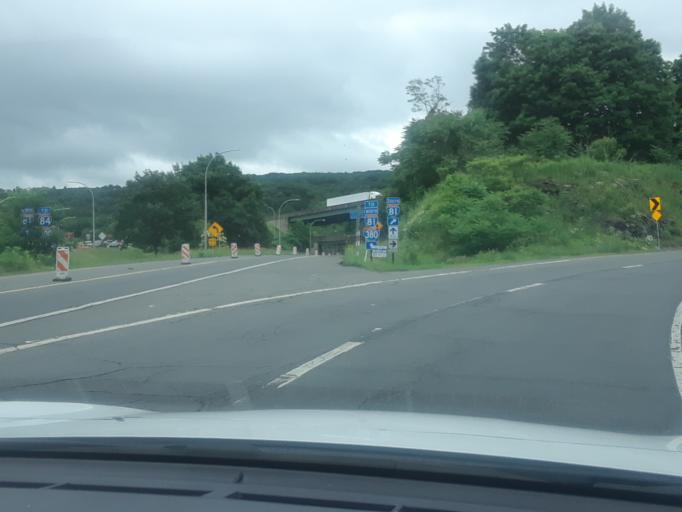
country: US
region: Pennsylvania
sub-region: Lackawanna County
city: Scranton
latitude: 41.3973
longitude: -75.6480
